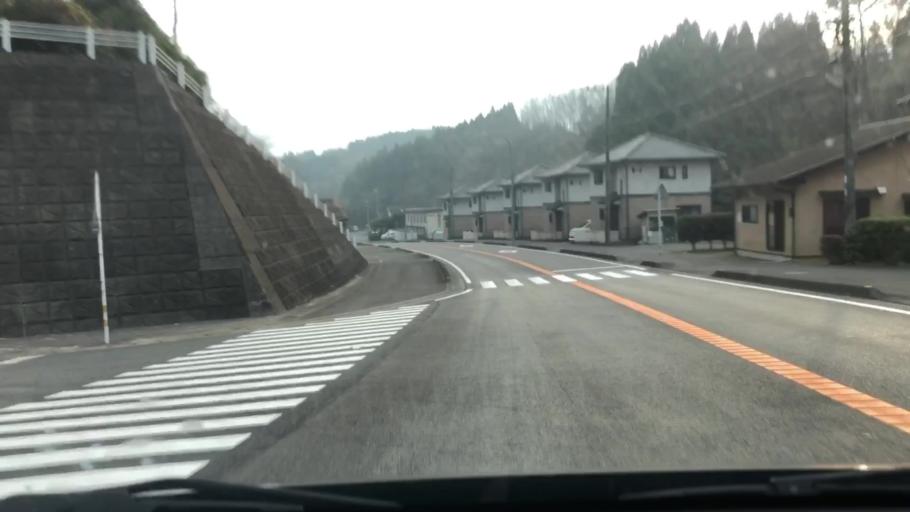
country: JP
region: Oita
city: Takedamachi
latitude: 32.9734
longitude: 131.5212
